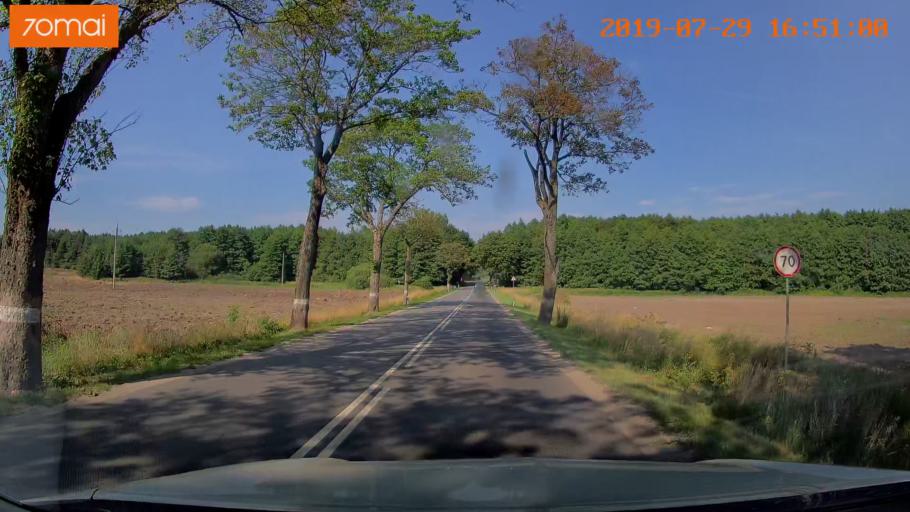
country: RU
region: Kaliningrad
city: Primorsk
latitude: 54.8057
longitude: 20.0618
